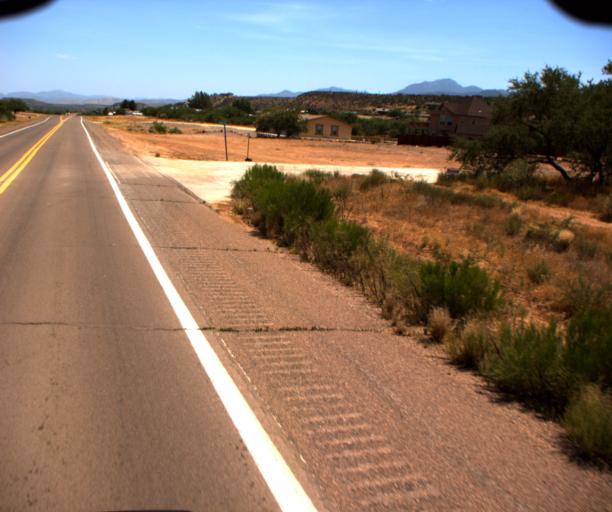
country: US
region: Arizona
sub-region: Gila County
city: Tonto Basin
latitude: 33.8479
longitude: -111.3090
